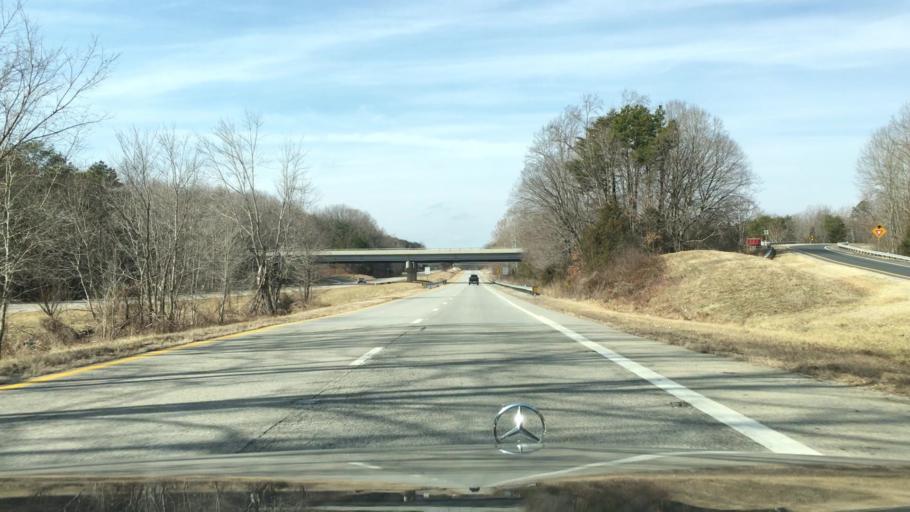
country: US
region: Virginia
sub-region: Prince Edward County
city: Farmville
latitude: 37.3120
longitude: -78.4587
